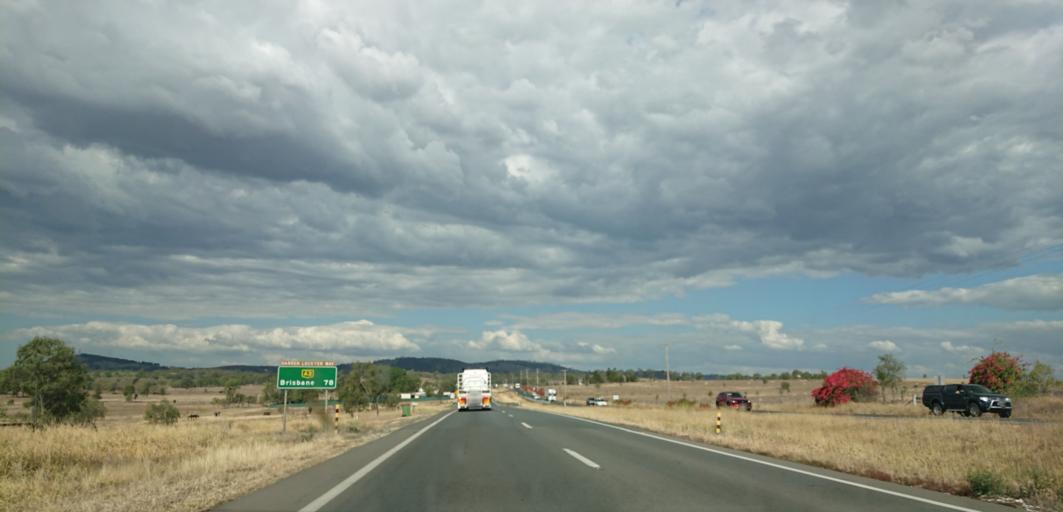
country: AU
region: Queensland
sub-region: Lockyer Valley
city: Gatton
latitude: -27.5556
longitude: 152.3939
